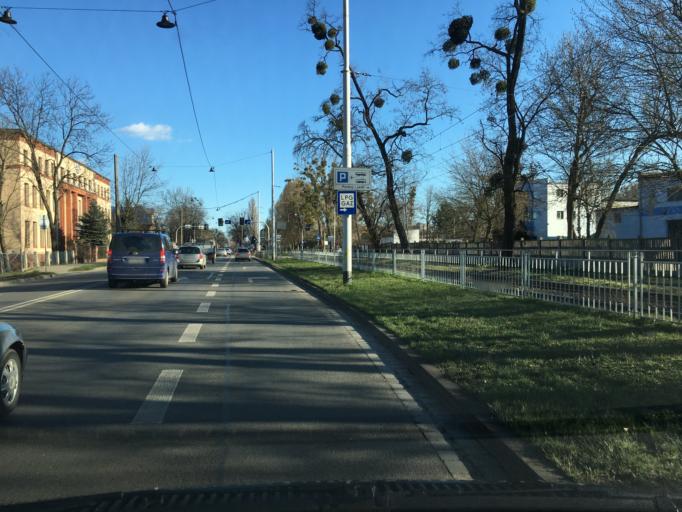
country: PL
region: Lower Silesian Voivodeship
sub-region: Powiat wroclawski
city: Radwanice
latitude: 51.0825
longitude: 17.0763
